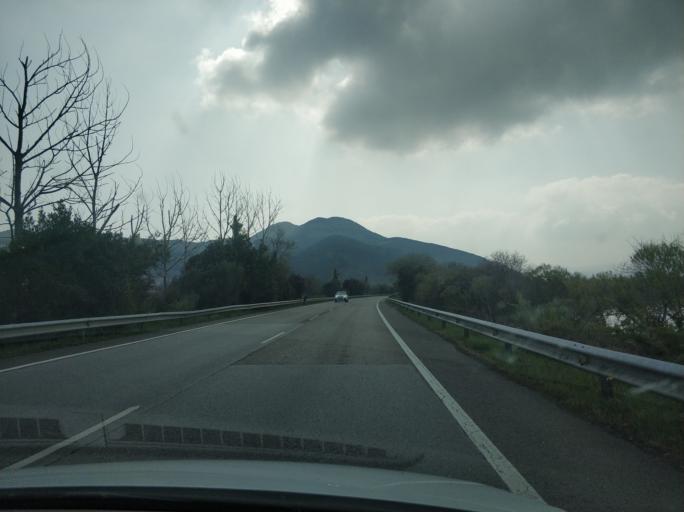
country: ES
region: Cantabria
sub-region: Provincia de Cantabria
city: Santona
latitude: 43.4594
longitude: -3.4675
